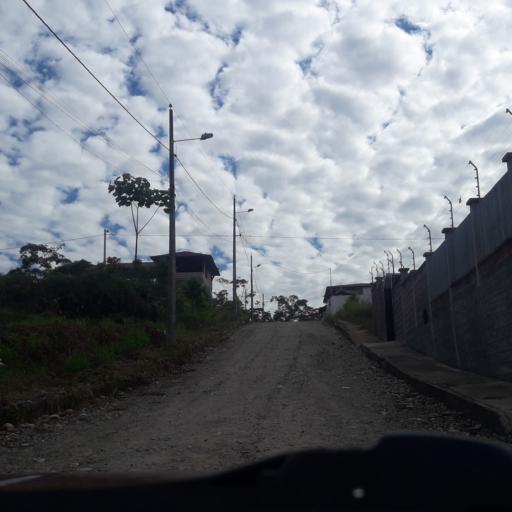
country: EC
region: Napo
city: Tena
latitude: -0.9823
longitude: -77.8247
